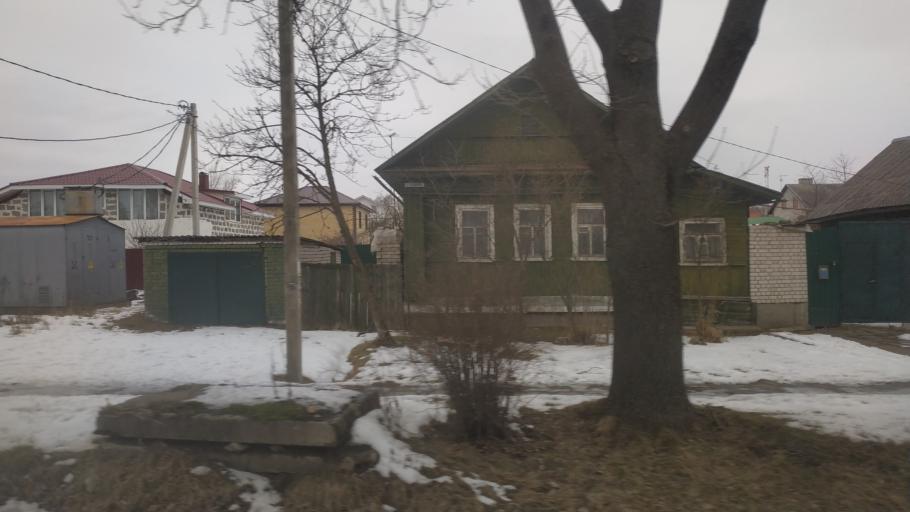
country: RU
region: Tverskaya
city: Tver
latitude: 56.8909
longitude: 35.8639
